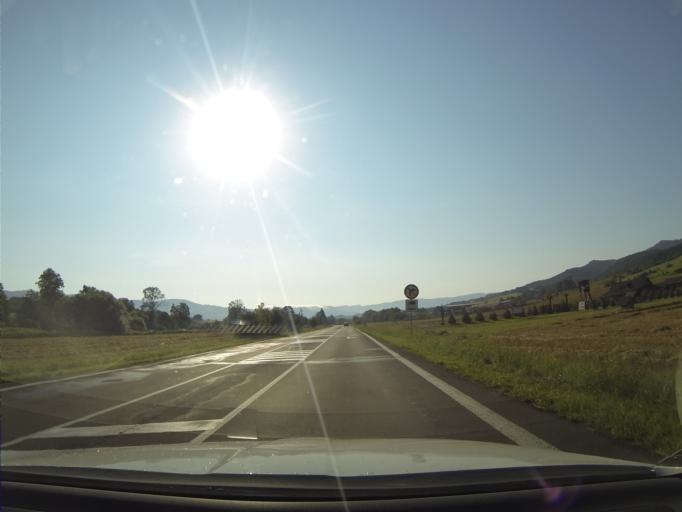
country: SK
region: Nitriansky
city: Prievidza
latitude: 48.7822
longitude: 18.6827
